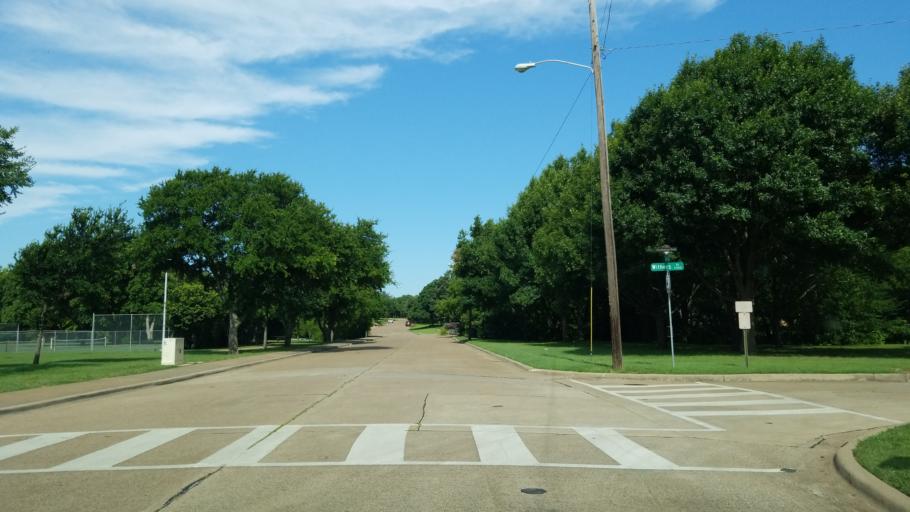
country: US
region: Texas
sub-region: Dallas County
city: Farmers Branch
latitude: 32.9043
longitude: -96.8475
